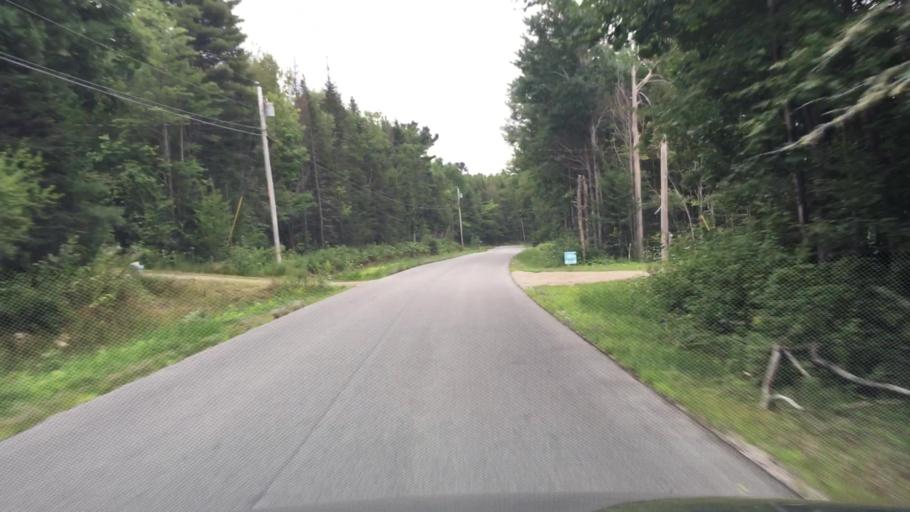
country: US
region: Maine
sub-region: Waldo County
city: Stockton Springs
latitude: 44.5141
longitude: -68.8753
